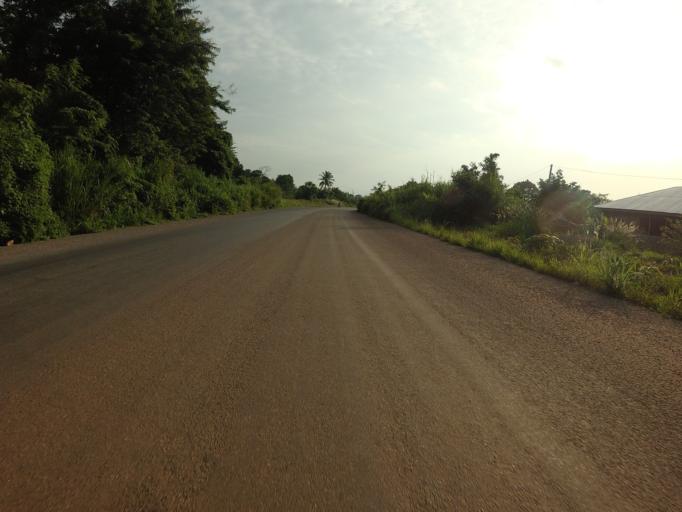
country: GH
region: Volta
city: Kpandu
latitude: 6.9138
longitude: 0.4535
